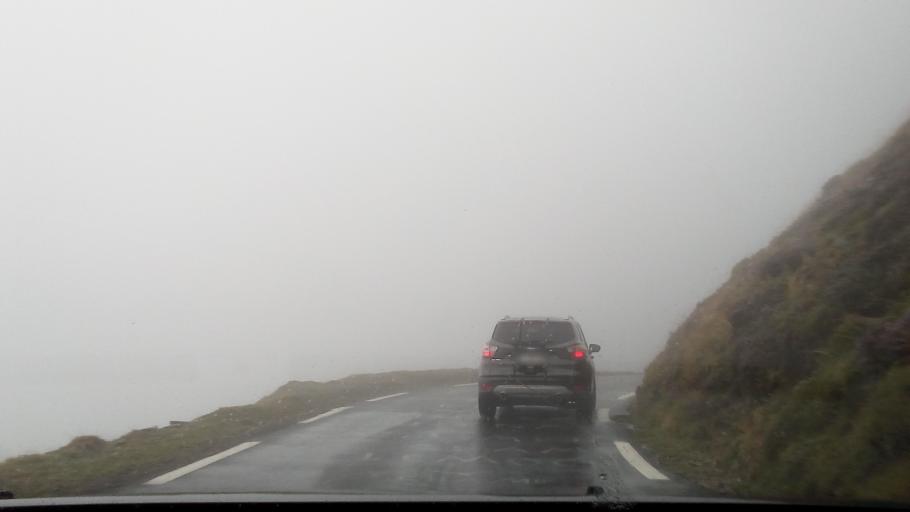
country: FR
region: Midi-Pyrenees
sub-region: Departement des Hautes-Pyrenees
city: Campan
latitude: 42.9105
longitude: 0.1380
